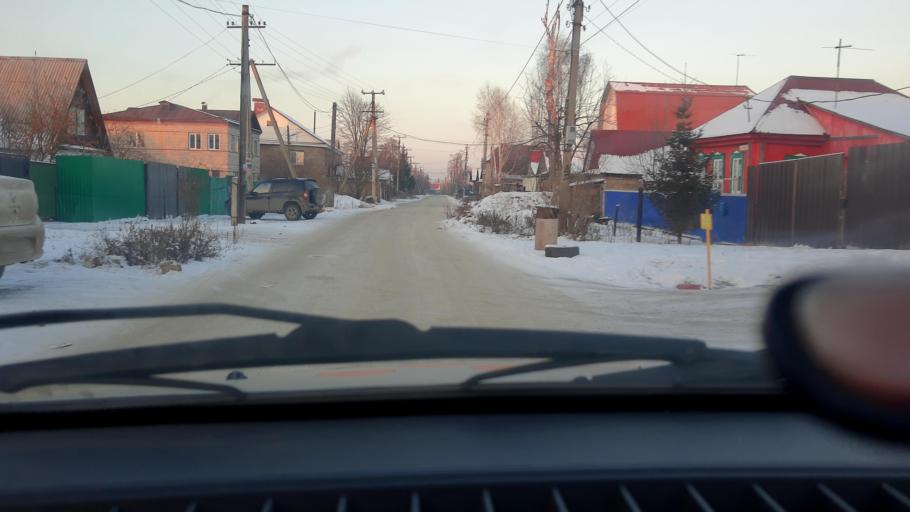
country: RU
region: Bashkortostan
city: Iglino
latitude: 54.8208
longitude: 56.1856
